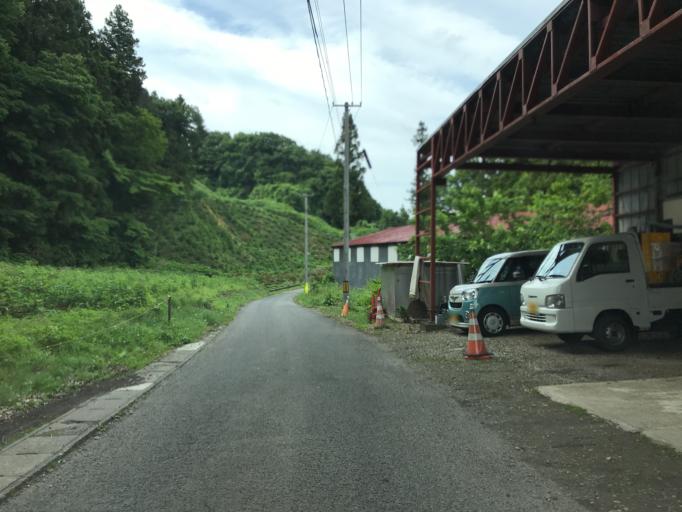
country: JP
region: Fukushima
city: Funehikimachi-funehiki
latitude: 37.5078
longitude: 140.6498
